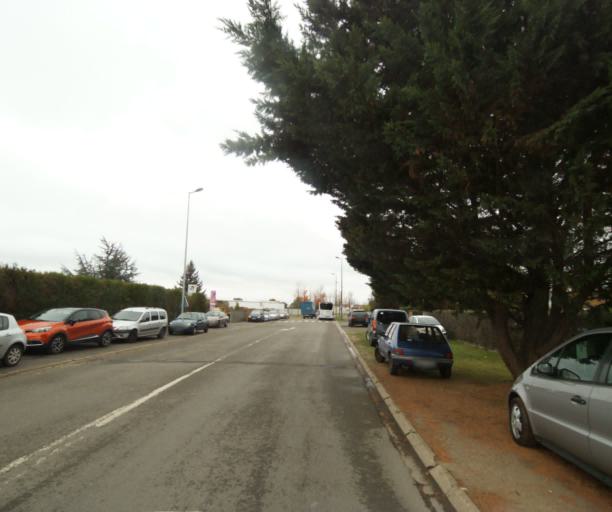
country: FR
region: Centre
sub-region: Departement d'Eure-et-Loir
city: Dreux
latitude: 48.7505
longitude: 1.3607
